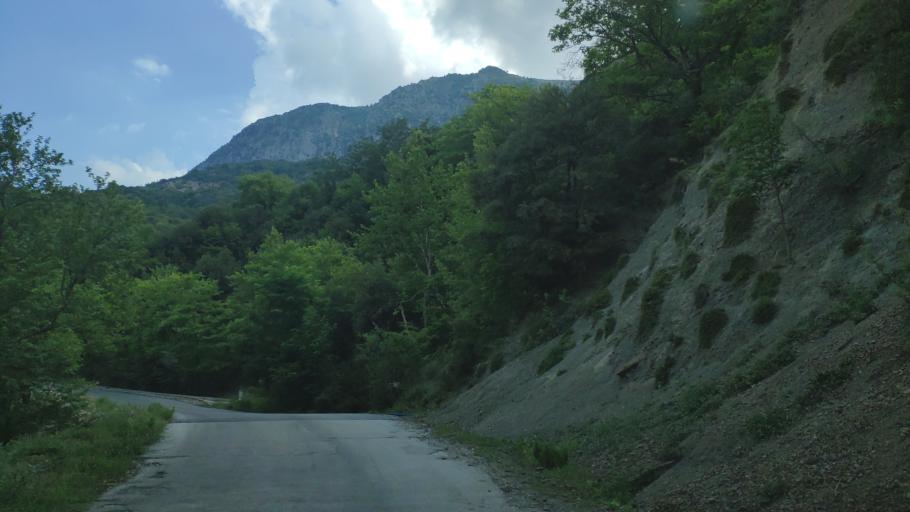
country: GR
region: Epirus
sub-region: Nomos Artas
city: Agios Dimitrios
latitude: 39.3920
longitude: 21.0198
